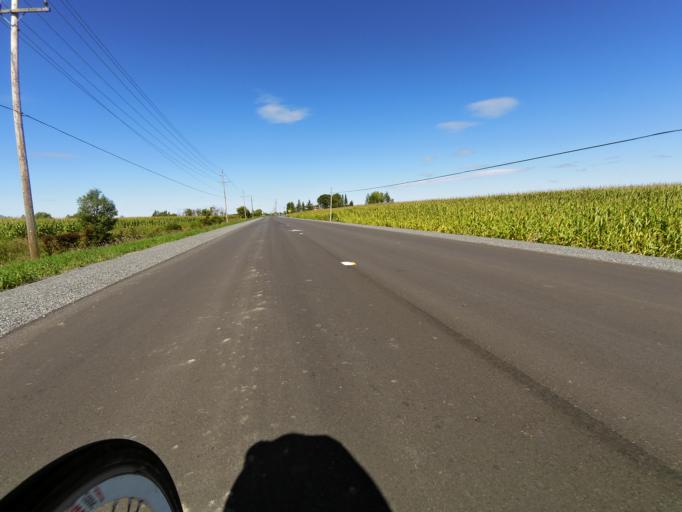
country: CA
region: Ontario
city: Bells Corners
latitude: 45.2264
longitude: -75.8603
